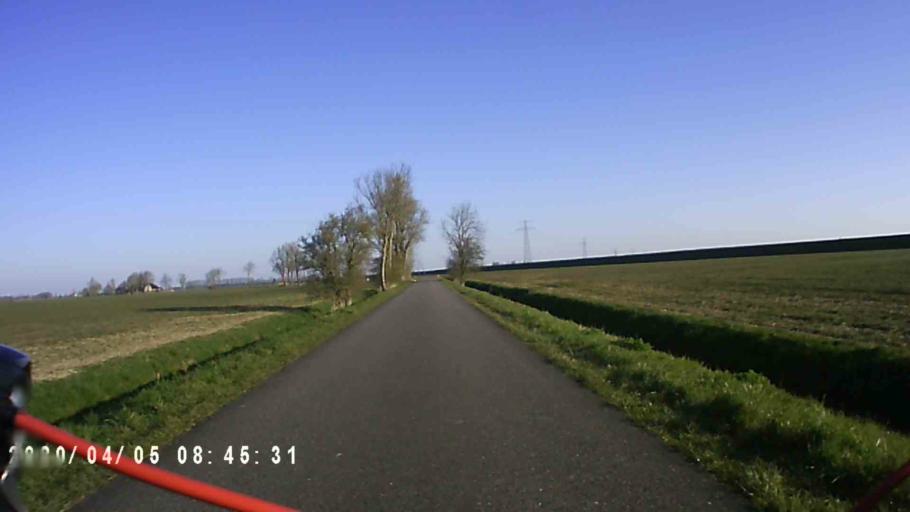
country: NL
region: Groningen
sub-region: Gemeente Winsum
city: Winsum
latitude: 53.3083
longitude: 6.4879
